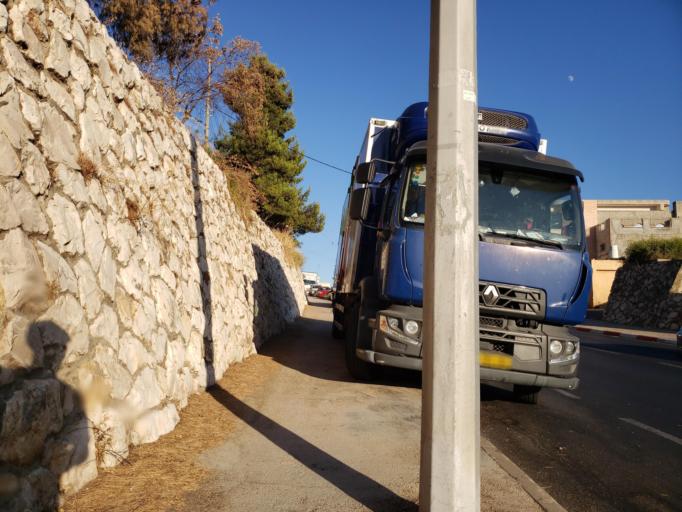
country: IL
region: Northern District
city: Safed
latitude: 32.9576
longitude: 35.4935
